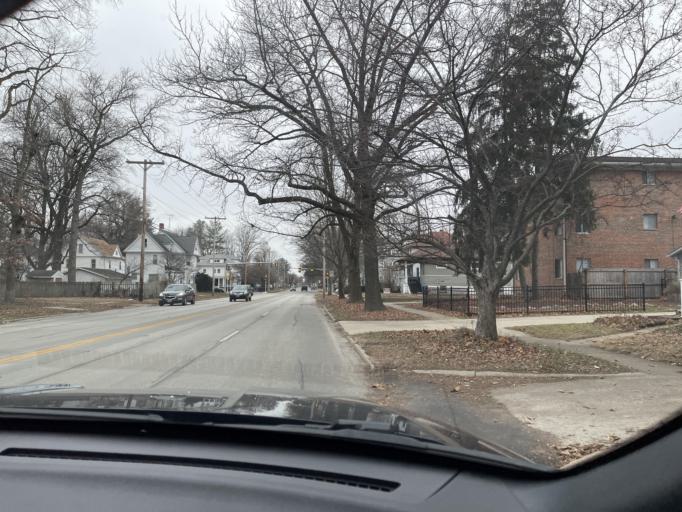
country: US
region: Illinois
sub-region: Sangamon County
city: Springfield
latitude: 39.7943
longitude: -89.6618
